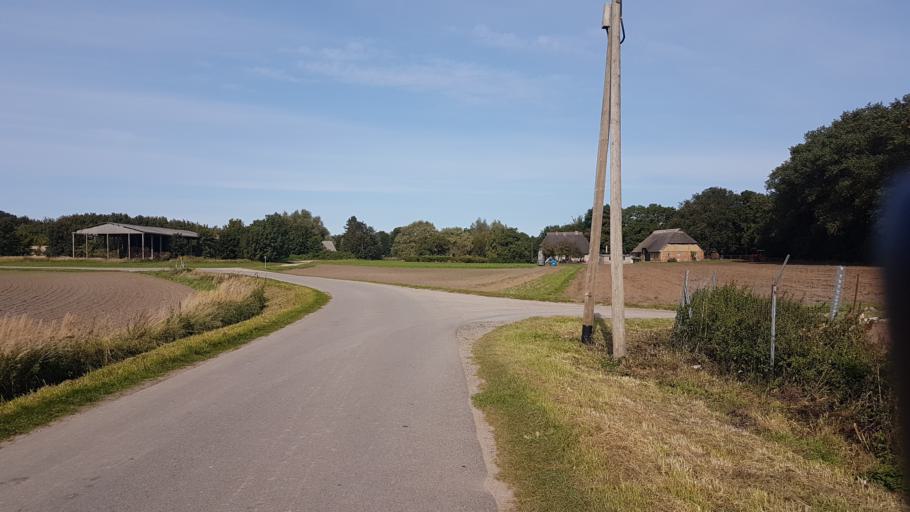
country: DE
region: Mecklenburg-Vorpommern
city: Gingst
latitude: 54.4340
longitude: 13.2242
